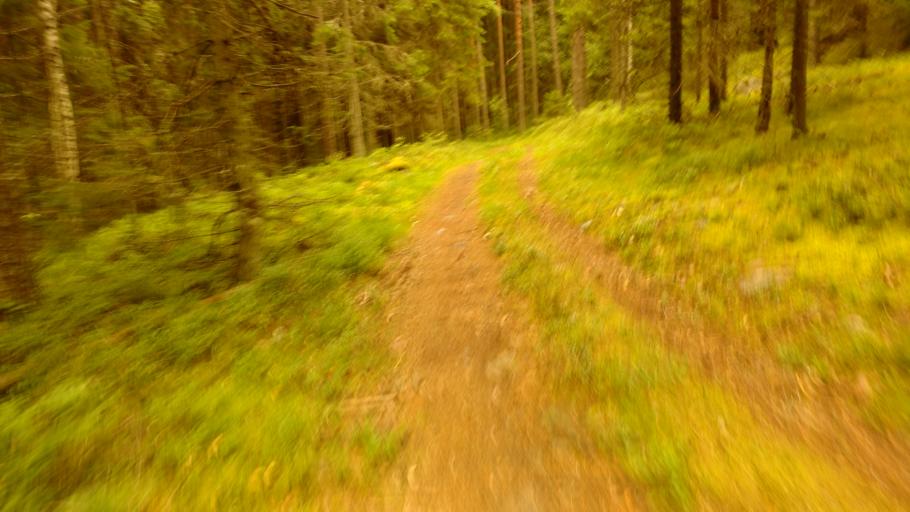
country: FI
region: Varsinais-Suomi
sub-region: Salo
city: Pertteli
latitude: 60.4026
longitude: 23.2187
